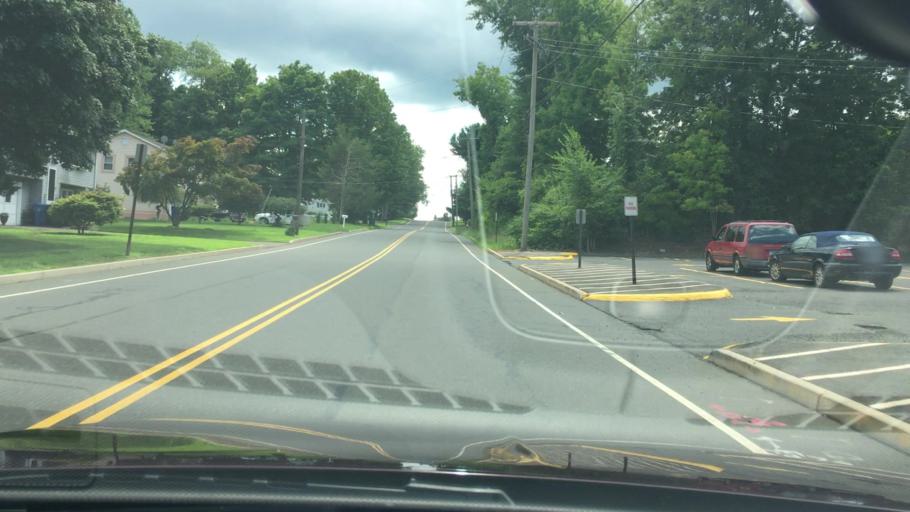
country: US
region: Connecticut
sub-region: Hartford County
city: Kensington
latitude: 41.6465
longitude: -72.7362
